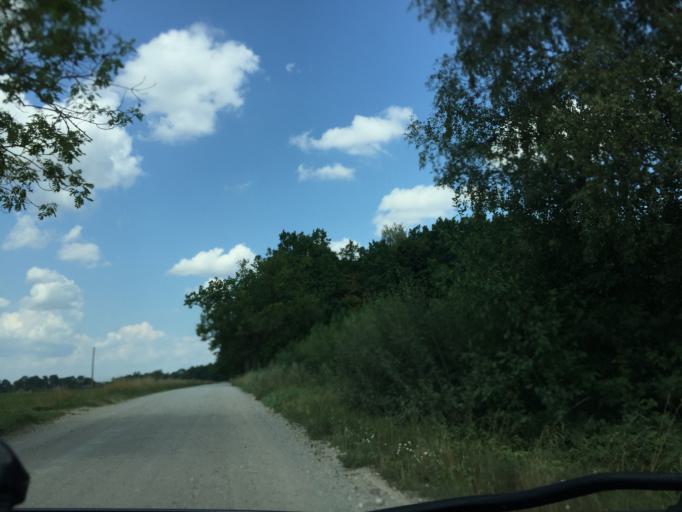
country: LT
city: Zagare
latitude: 56.3911
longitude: 23.2546
